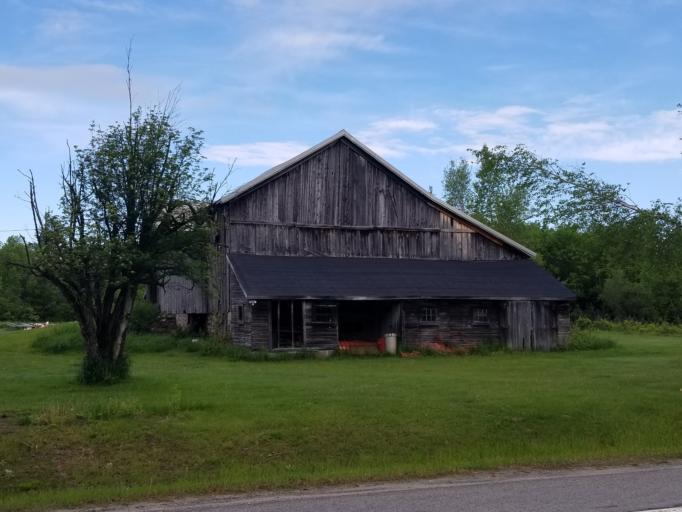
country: US
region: New York
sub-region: Herkimer County
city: Herkimer
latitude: 43.3088
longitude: -74.9705
